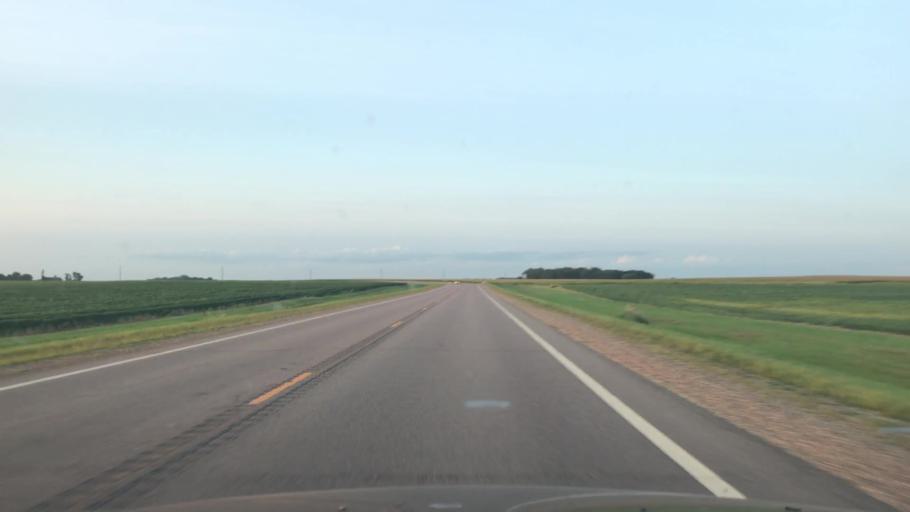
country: US
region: Minnesota
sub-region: Redwood County
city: Redwood Falls
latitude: 44.4161
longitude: -95.1235
